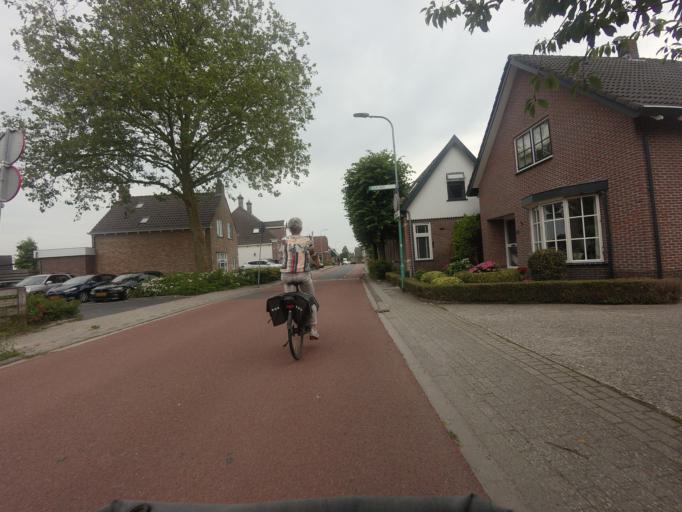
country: NL
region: North Holland
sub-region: Gemeente Enkhuizen
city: Enkhuizen
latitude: 52.6978
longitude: 5.1988
